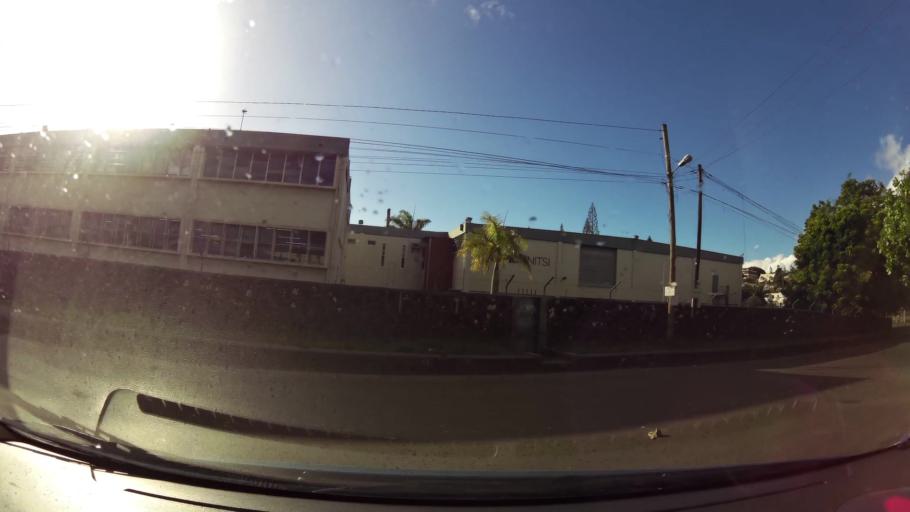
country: MU
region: Plaines Wilhems
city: Vacoas
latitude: -20.3104
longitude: 57.4950
